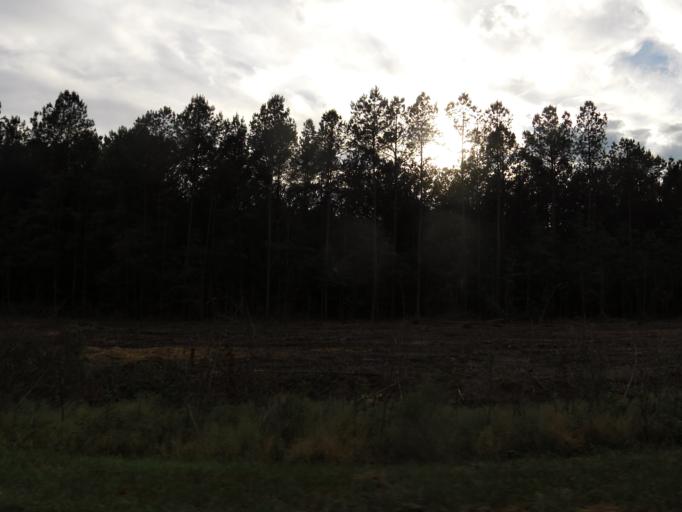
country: US
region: South Carolina
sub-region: Jasper County
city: Ridgeland
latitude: 32.4312
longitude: -81.1034
